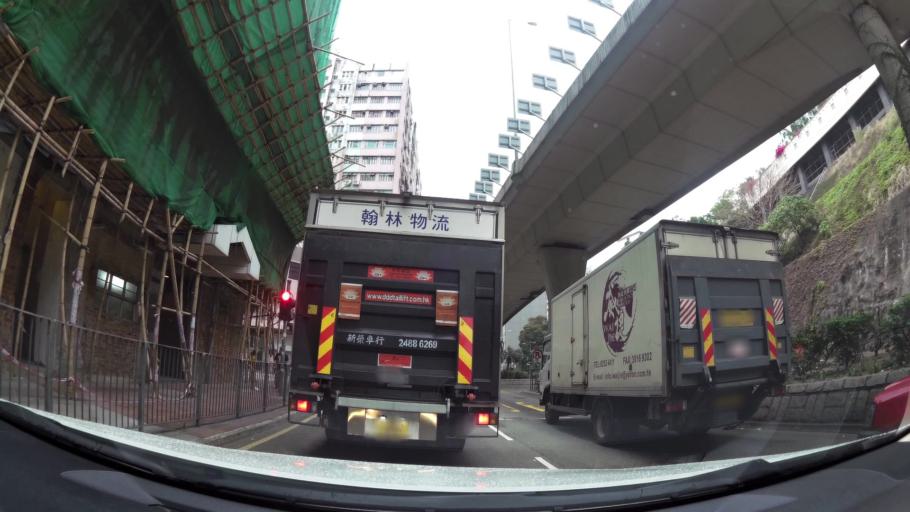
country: HK
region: Tsuen Wan
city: Tsuen Wan
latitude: 22.3668
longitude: 114.1214
